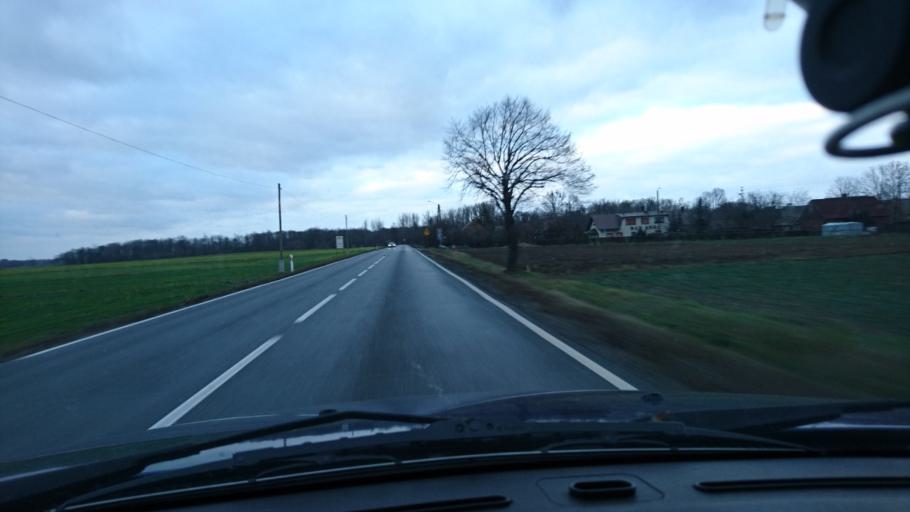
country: PL
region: Opole Voivodeship
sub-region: Powiat kluczborski
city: Byczyna
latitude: 51.1397
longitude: 18.1960
